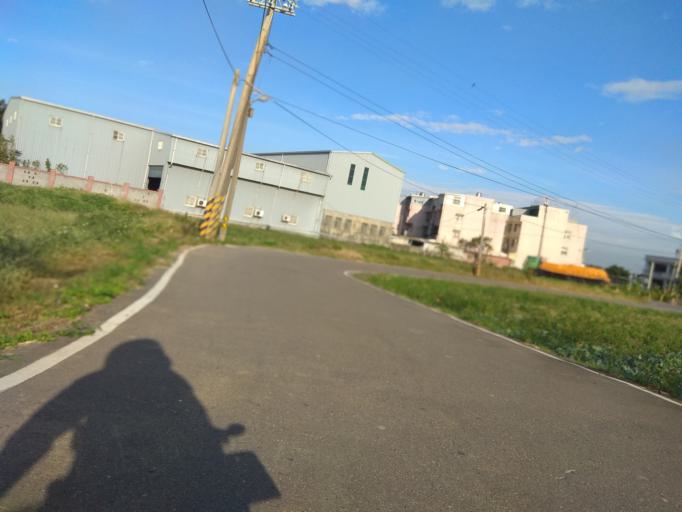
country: TW
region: Taiwan
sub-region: Hsinchu
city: Zhubei
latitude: 24.9812
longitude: 121.0545
